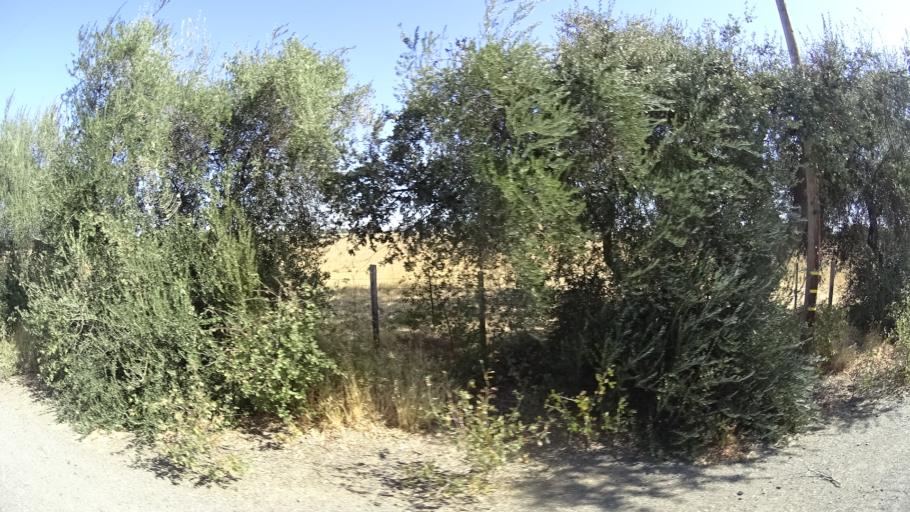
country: US
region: California
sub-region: Solano County
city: Dixon
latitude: 38.5410
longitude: -121.8530
